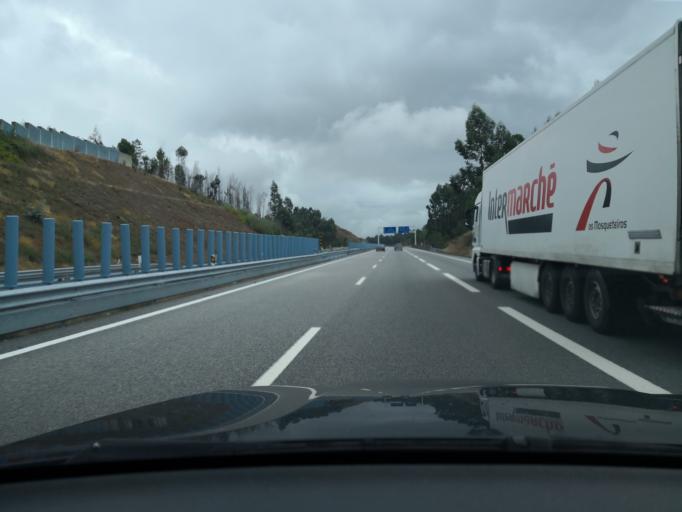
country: PT
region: Porto
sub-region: Lousada
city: Lousada
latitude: 41.2946
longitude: -8.2961
